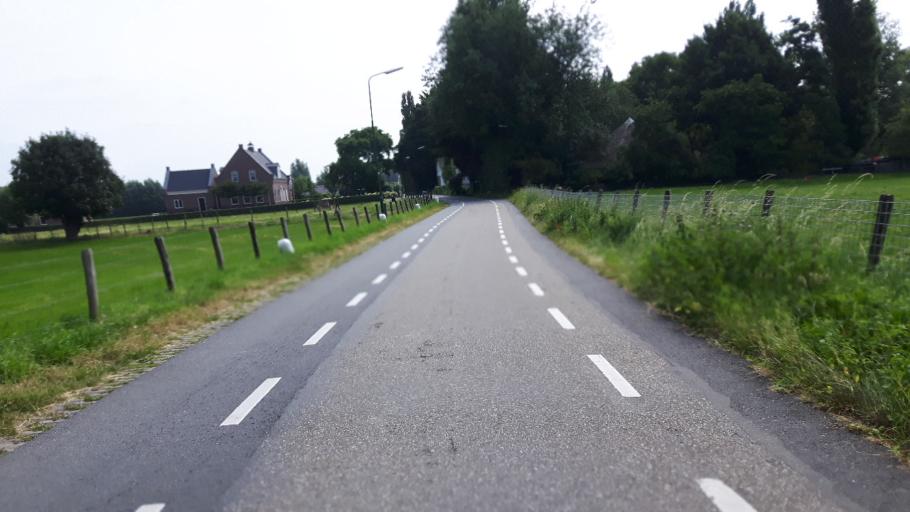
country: NL
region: Utrecht
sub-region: Gemeente Montfoort
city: Montfoort
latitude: 52.0572
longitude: 4.9827
